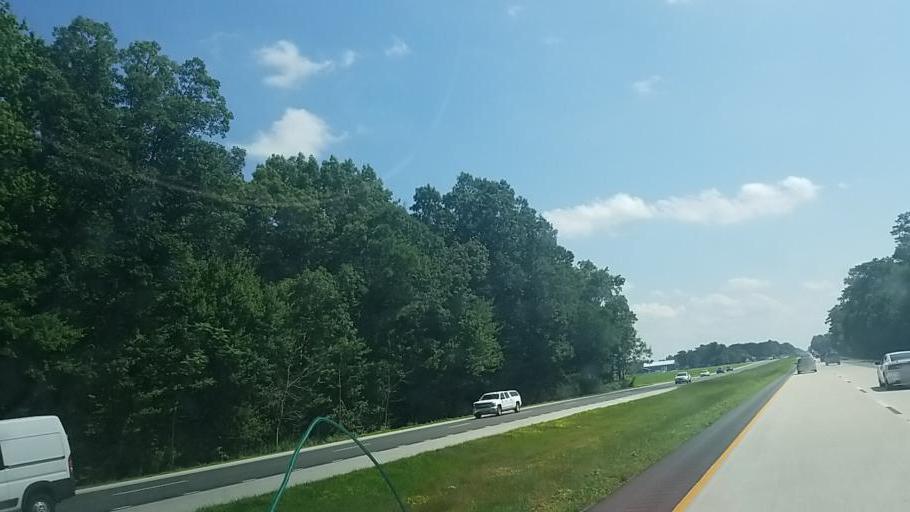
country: US
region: Delaware
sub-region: Sussex County
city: Milford
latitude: 38.8610
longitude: -75.4394
